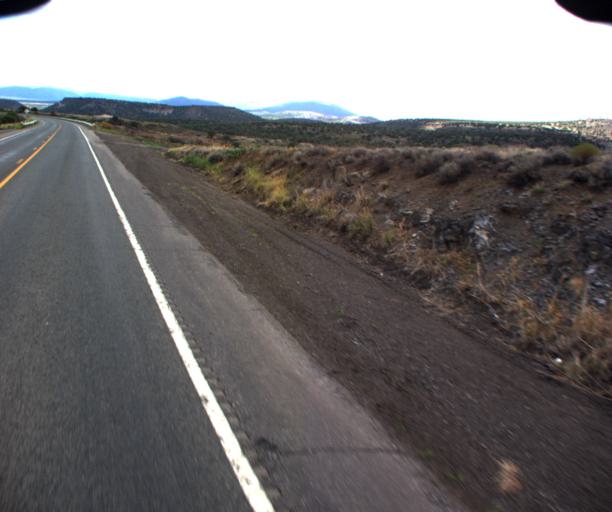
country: US
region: Arizona
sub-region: Yavapai County
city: Camp Verde
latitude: 34.5160
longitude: -112.0229
